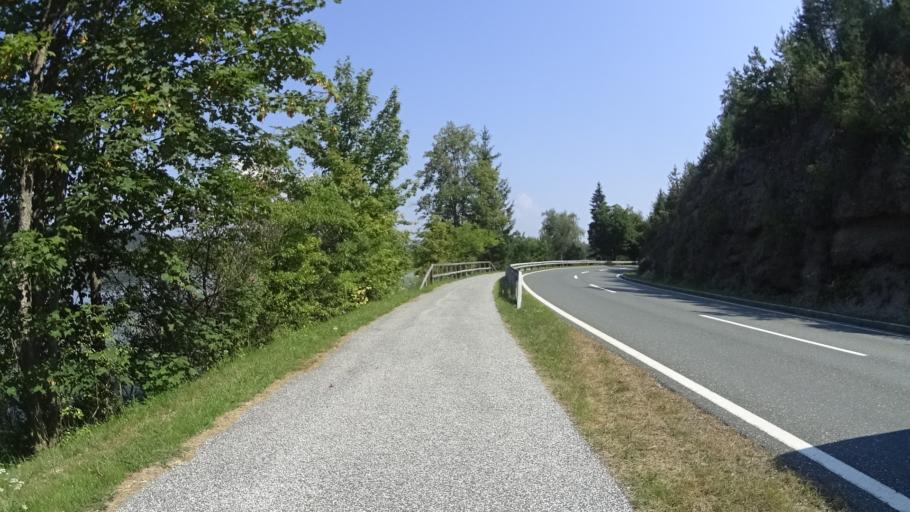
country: AT
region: Carinthia
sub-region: Politischer Bezirk Volkermarkt
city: Sittersdorf
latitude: 46.5630
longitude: 14.6249
